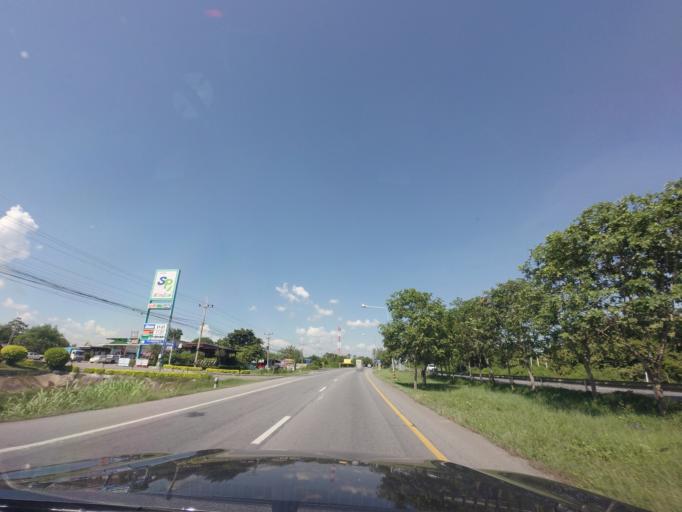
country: TH
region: Nakhon Ratchasima
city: Non Sung
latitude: 15.2224
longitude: 102.3627
